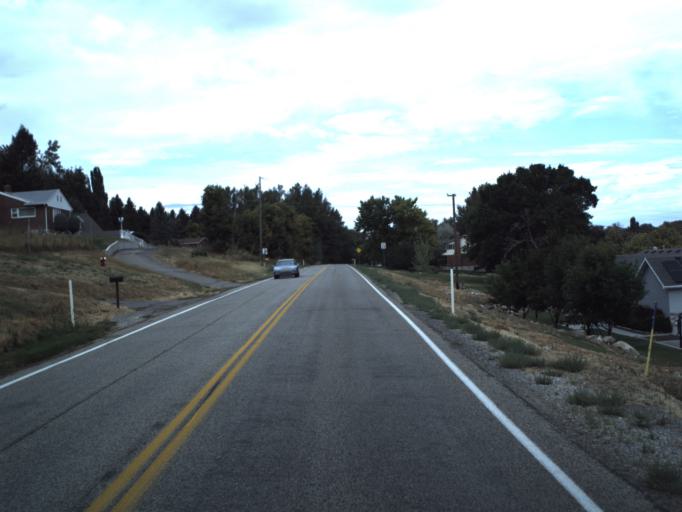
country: US
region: Utah
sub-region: Cache County
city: Mendon
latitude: 41.7007
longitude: -111.9770
